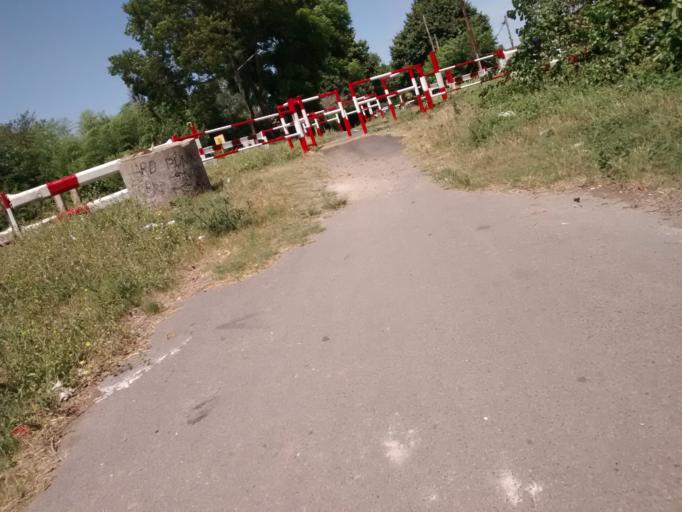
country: AR
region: Buenos Aires
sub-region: Partido de La Plata
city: La Plata
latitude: -34.8821
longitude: -58.0042
